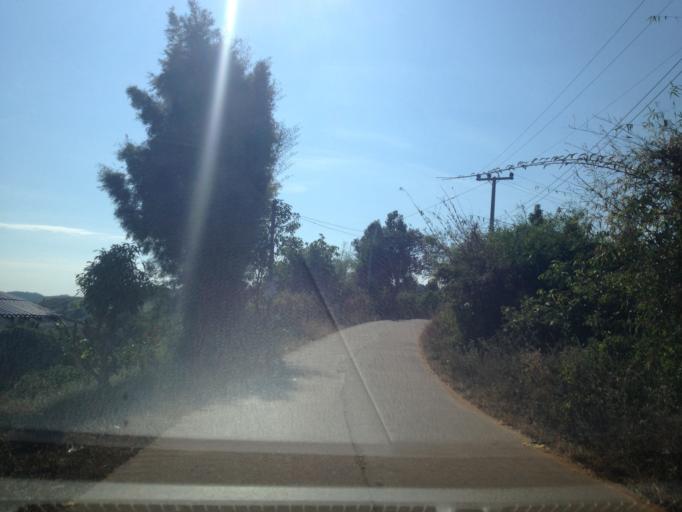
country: TH
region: Mae Hong Son
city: Ban Huai I Huak
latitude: 18.0440
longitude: 98.1655
